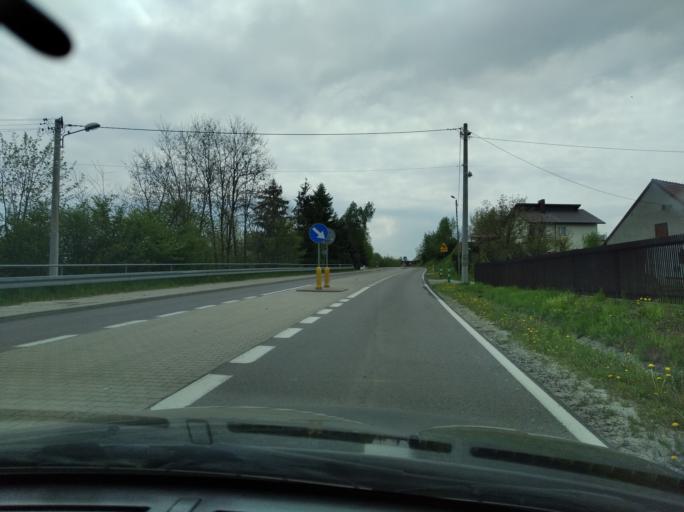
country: PL
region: Lesser Poland Voivodeship
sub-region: Powiat tarnowski
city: Tarnowiec
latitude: 49.9544
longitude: 21.0063
